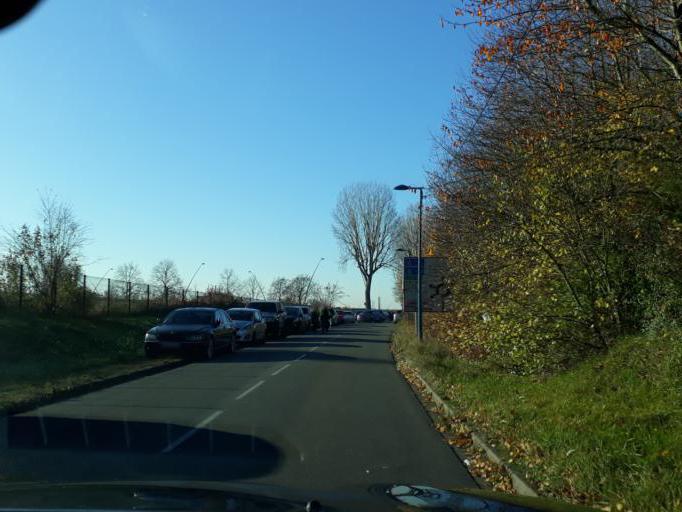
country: FR
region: Nord-Pas-de-Calais
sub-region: Departement du Nord
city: Dechy
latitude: 50.3479
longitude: 3.1178
